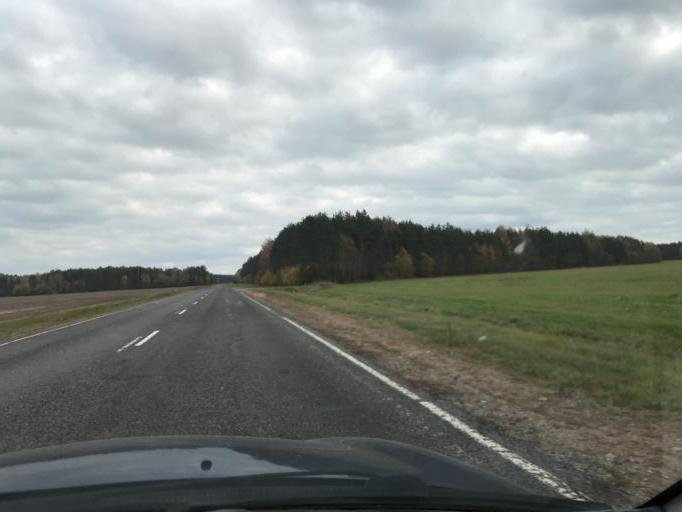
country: BY
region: Grodnenskaya
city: Lida
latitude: 53.7472
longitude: 25.2759
